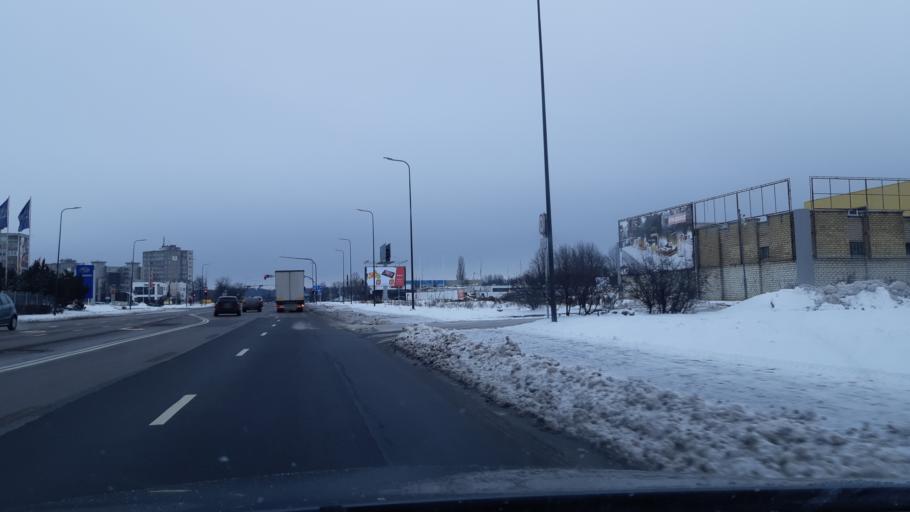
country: LT
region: Kauno apskritis
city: Dainava (Kaunas)
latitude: 54.9268
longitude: 23.9744
